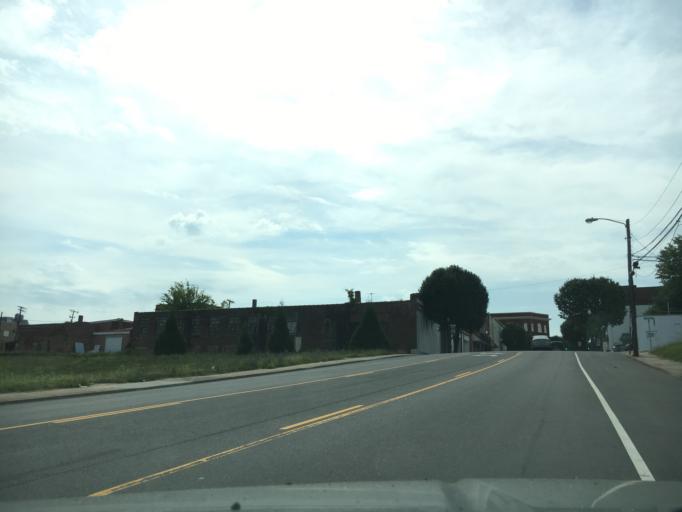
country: US
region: Virginia
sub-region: Halifax County
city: South Boston
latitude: 36.6998
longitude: -78.9031
